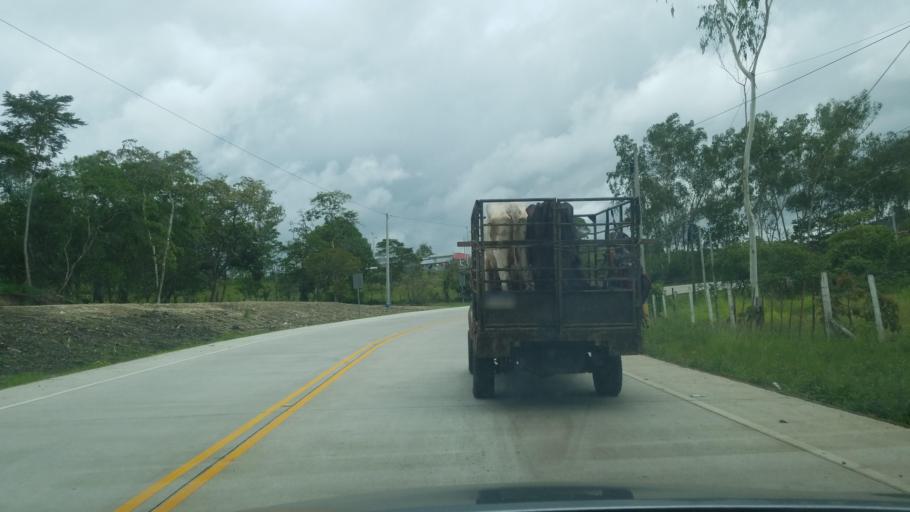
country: HN
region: Copan
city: San Jeronimo
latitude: 14.9776
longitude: -88.8826
